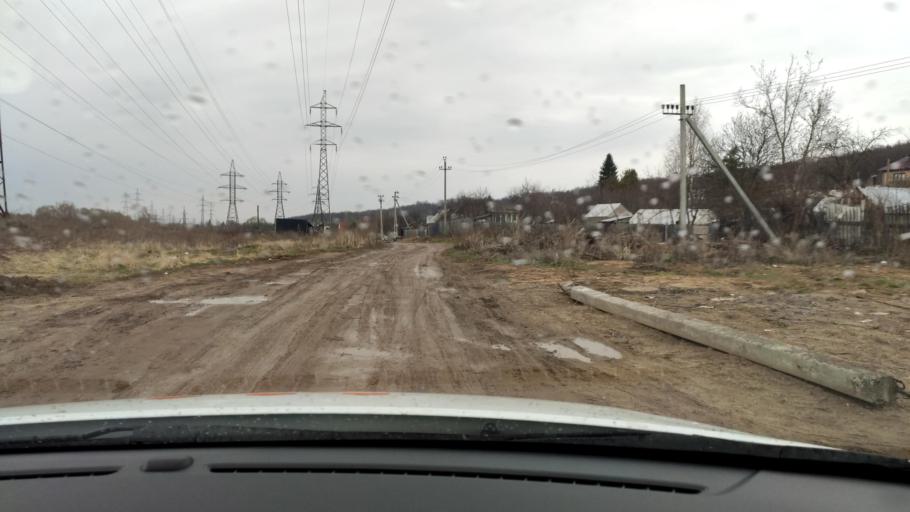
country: RU
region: Tatarstan
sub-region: Gorod Kazan'
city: Kazan
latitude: 55.8180
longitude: 49.2110
